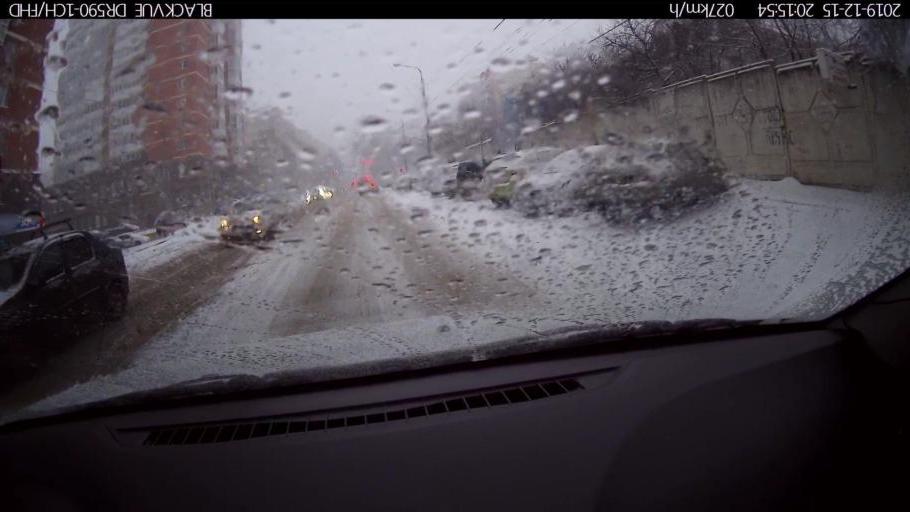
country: RU
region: Nizjnij Novgorod
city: Nizhniy Novgorod
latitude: 56.3132
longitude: 44.0300
